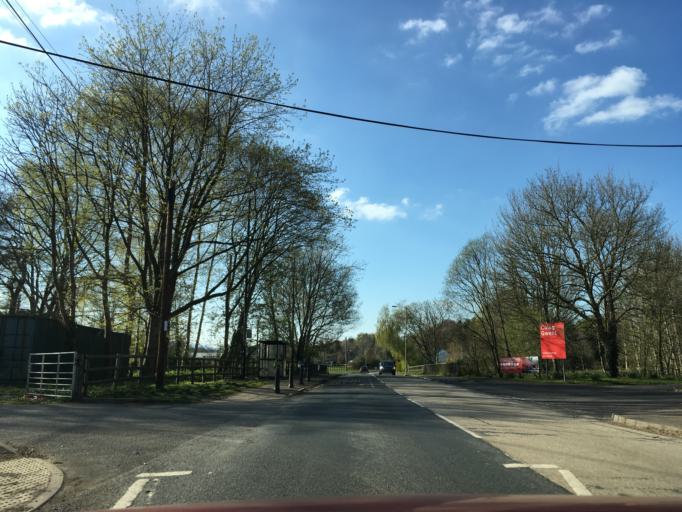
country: GB
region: Wales
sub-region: Monmouthshire
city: Usk
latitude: 51.7123
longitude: -2.9194
